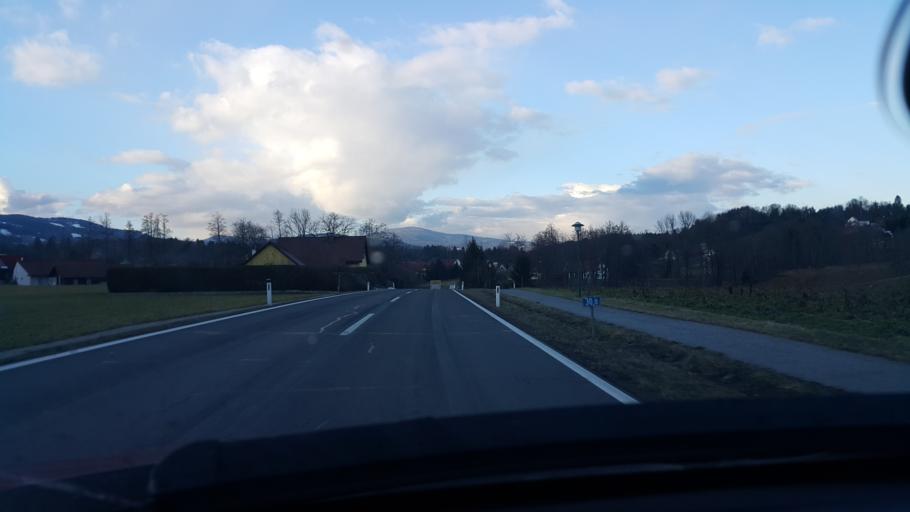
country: AT
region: Styria
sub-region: Politischer Bezirk Deutschlandsberg
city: Hollenegg
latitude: 46.7816
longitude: 15.2424
